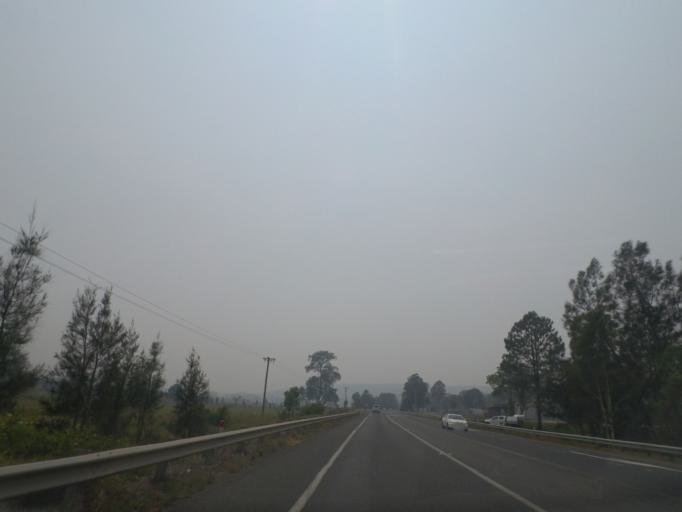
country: AU
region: New South Wales
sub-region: Clarence Valley
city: Maclean
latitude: -29.5658
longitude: 153.1379
